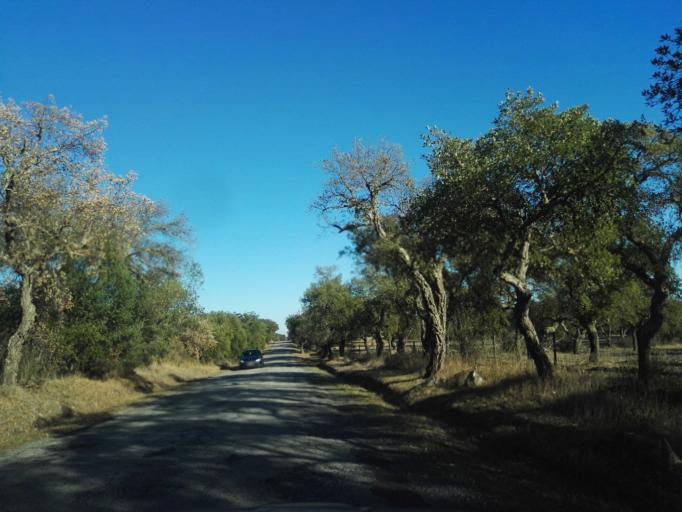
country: PT
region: Evora
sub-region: Arraiolos
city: Arraiolos
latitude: 38.7039
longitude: -7.8404
